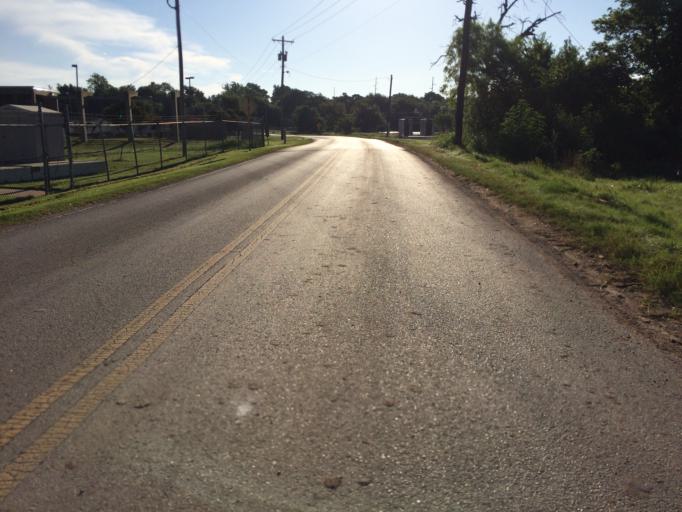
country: US
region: Oklahoma
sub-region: McClain County
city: Goldsby
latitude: 35.1741
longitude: -97.4438
